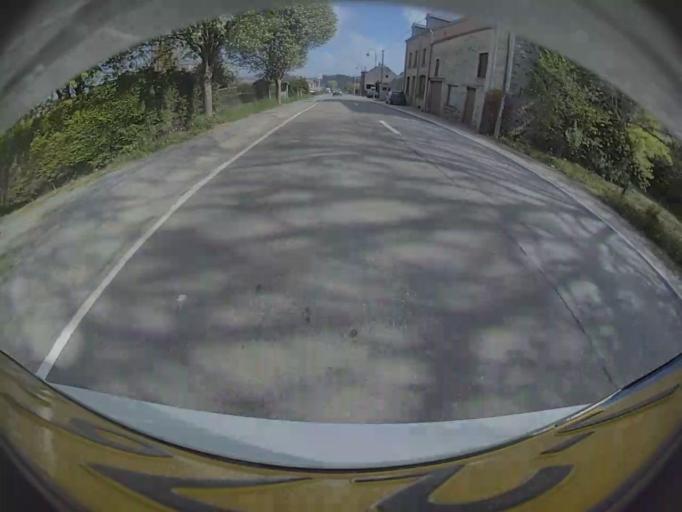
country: BE
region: Wallonia
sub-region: Province du Luxembourg
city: Tellin
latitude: 50.0833
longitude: 5.2219
